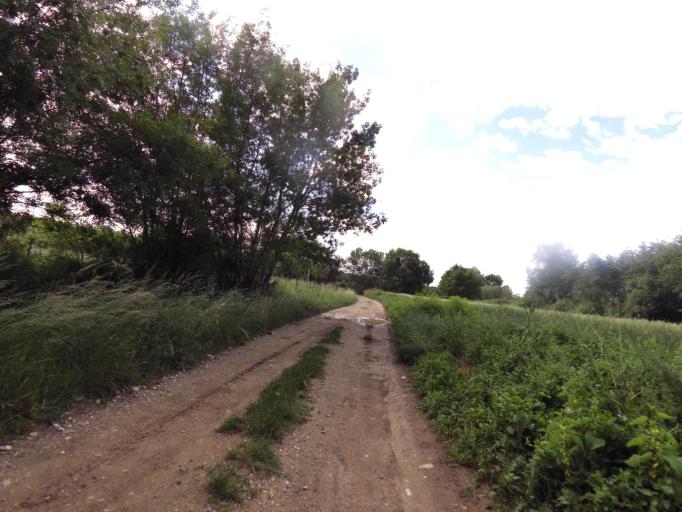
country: FR
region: Languedoc-Roussillon
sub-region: Departement du Gard
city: Vergeze
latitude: 43.7616
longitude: 4.2133
